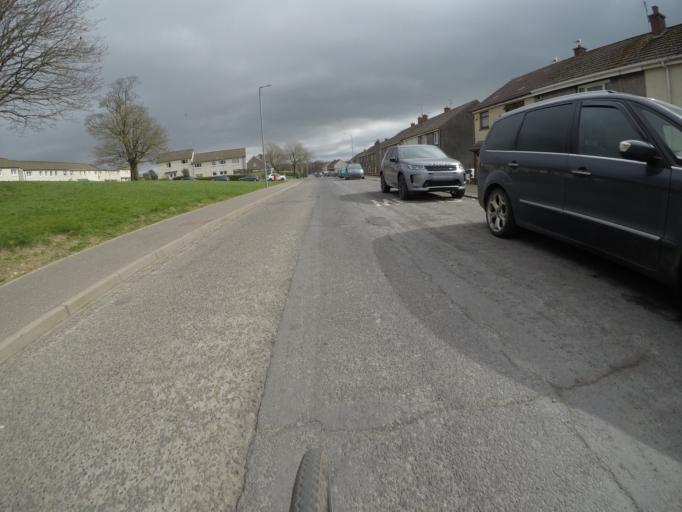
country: GB
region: Scotland
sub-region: East Ayrshire
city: Stewarton
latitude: 55.6791
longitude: -4.5258
